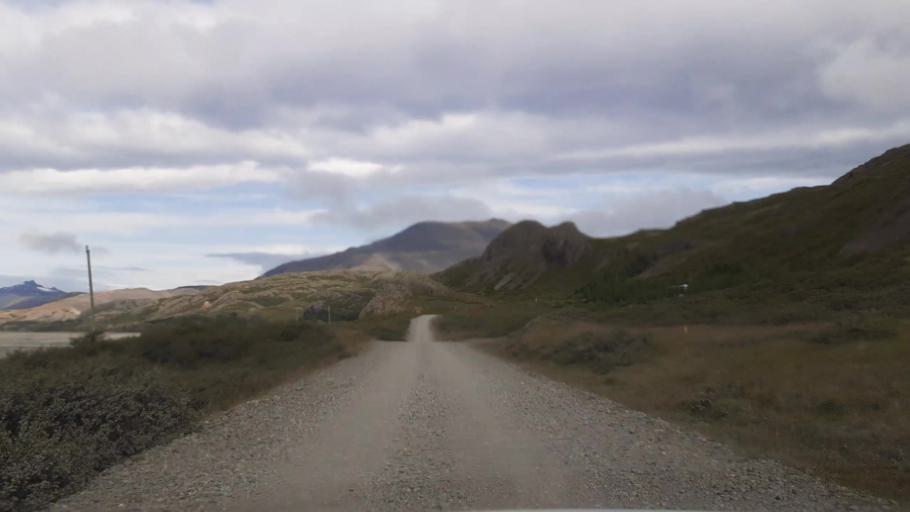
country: IS
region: East
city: Hoefn
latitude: 64.4269
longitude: -14.8837
